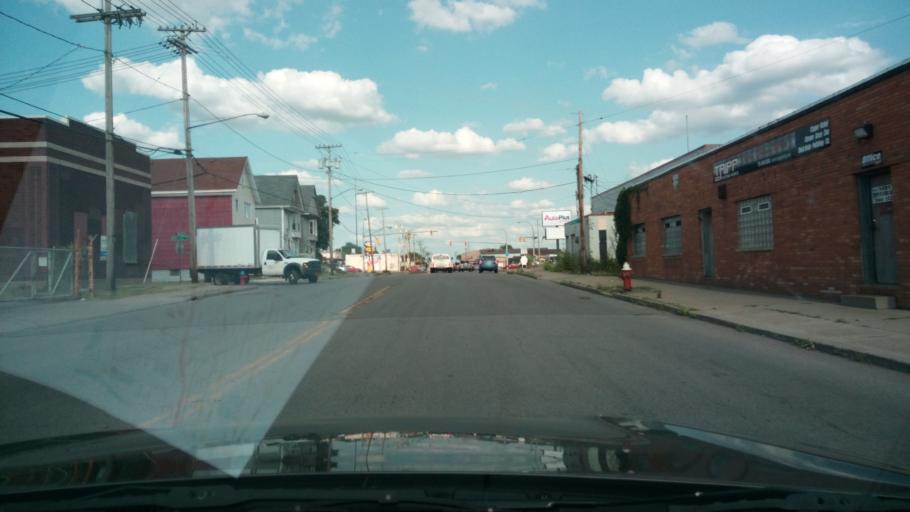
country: US
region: New York
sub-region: Erie County
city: Sloan
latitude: 42.8848
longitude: -78.8159
